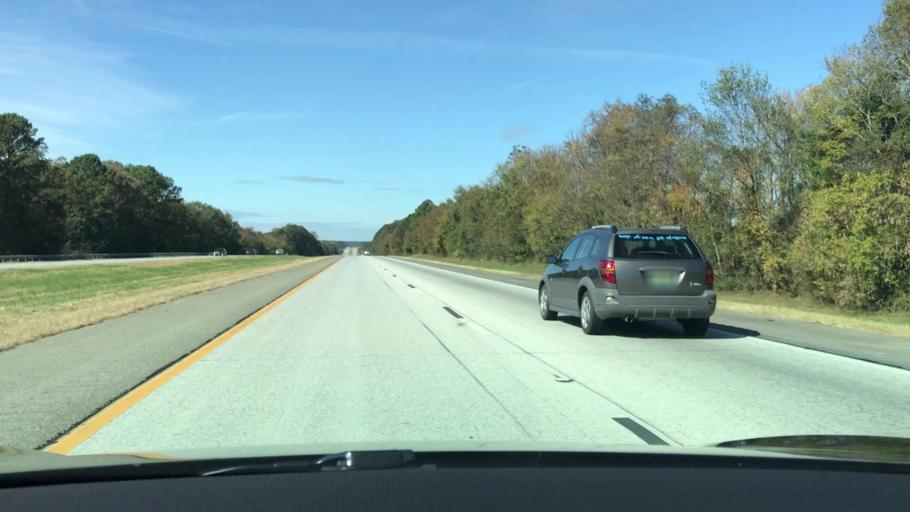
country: US
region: Georgia
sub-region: Putnam County
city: Jefferson
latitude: 33.5424
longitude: -83.3229
